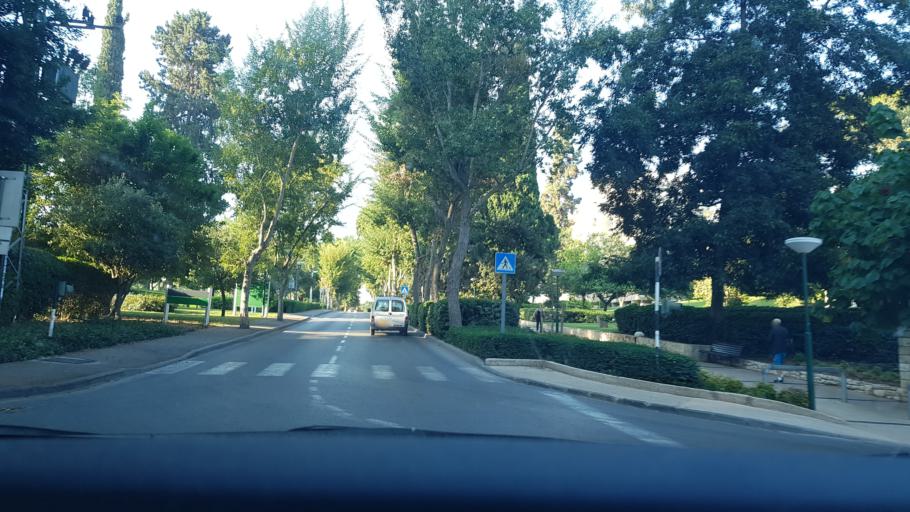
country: IL
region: Central District
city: Ness Ziona
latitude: 31.9067
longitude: 34.8111
